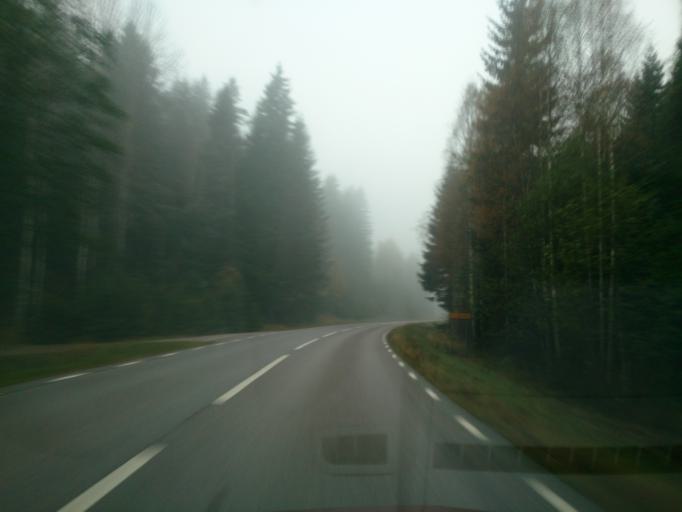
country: SE
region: OEstergoetland
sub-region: Atvidabergs Kommun
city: Atvidaberg
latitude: 58.0833
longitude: 15.9392
